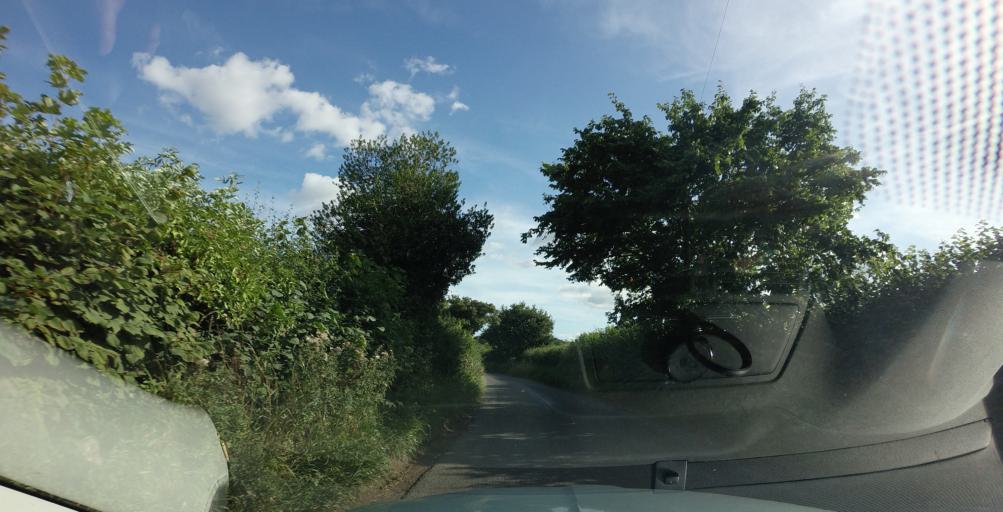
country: GB
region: England
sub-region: North Yorkshire
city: Ripon
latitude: 54.1047
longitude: -1.5169
